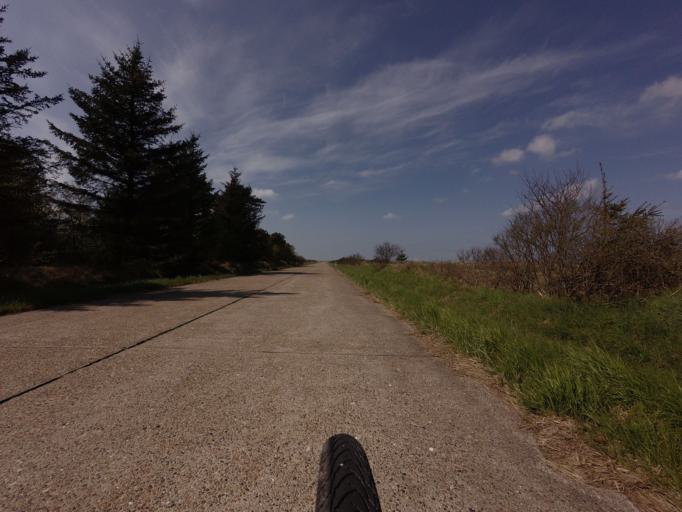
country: DK
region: North Denmark
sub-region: Jammerbugt Kommune
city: Brovst
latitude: 57.1719
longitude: 9.4604
